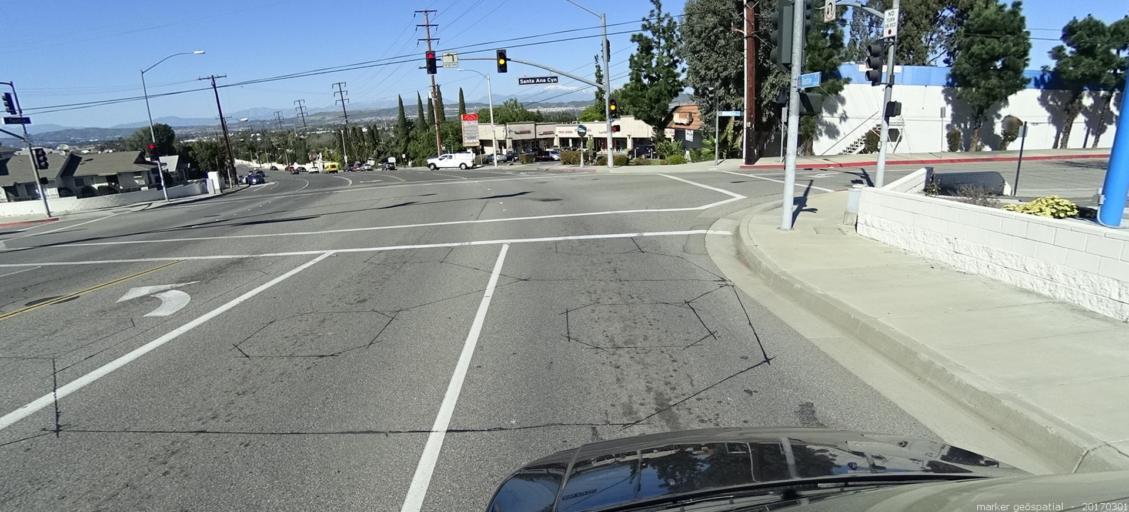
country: US
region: California
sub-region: Orange County
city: Villa Park
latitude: 33.8423
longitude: -117.8330
